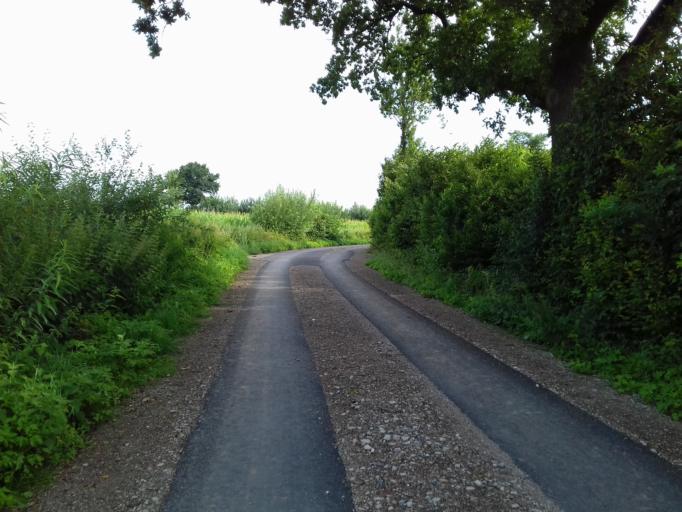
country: DE
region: Schleswig-Holstein
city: Bonebuttel
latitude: 54.0805
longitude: 10.0466
